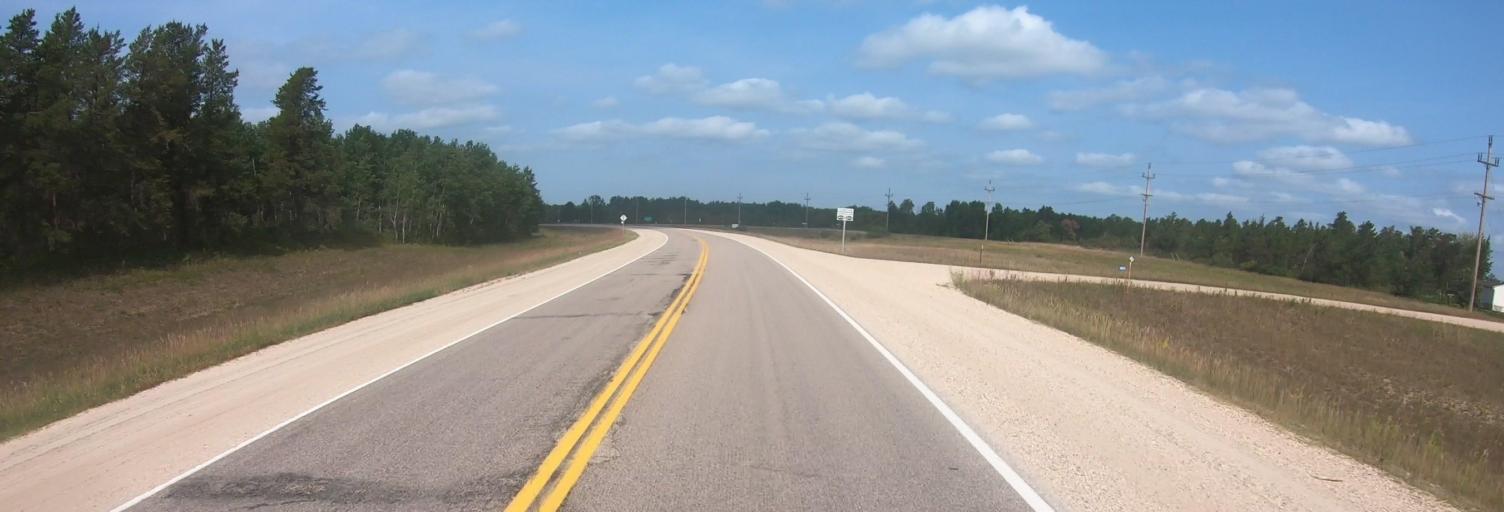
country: CA
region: Manitoba
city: La Broquerie
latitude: 49.2645
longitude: -96.3635
